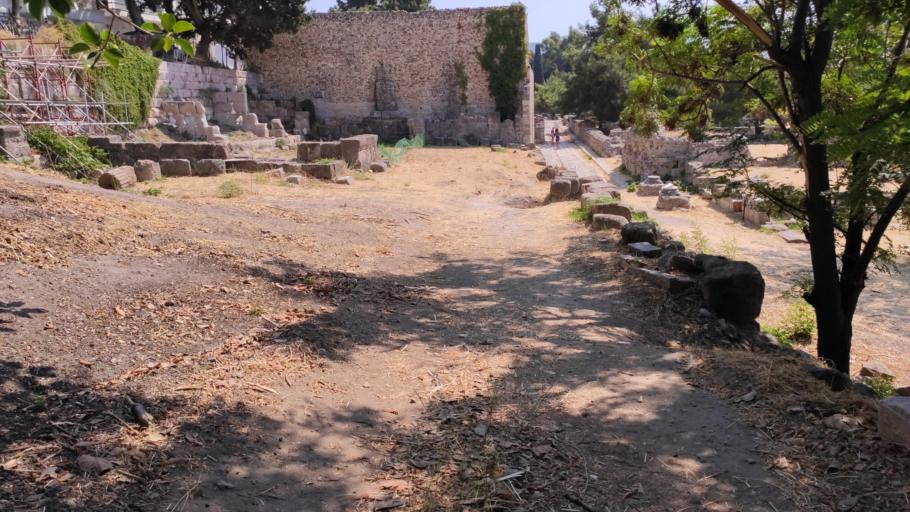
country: GR
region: South Aegean
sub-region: Nomos Dodekanisou
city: Kos
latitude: 36.8919
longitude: 27.2851
